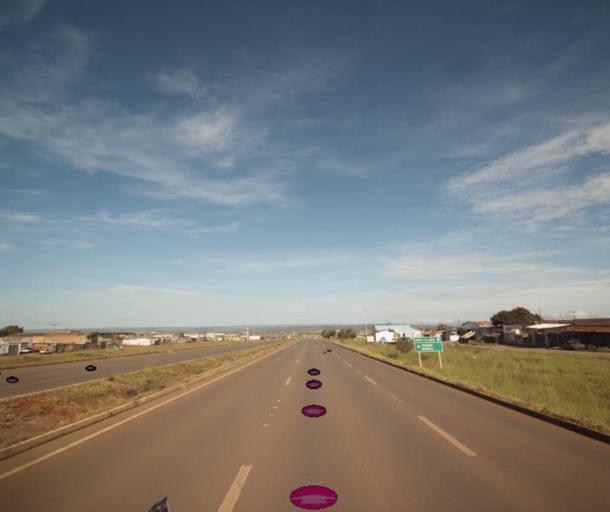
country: BR
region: Federal District
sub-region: Brasilia
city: Brasilia
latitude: -15.7376
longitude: -48.2935
